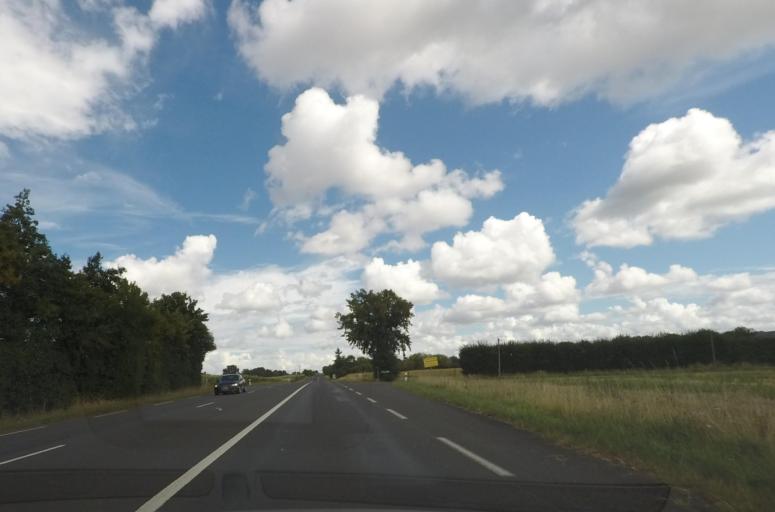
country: FR
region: Pays de la Loire
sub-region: Departement de la Sarthe
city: Clermont-Creans
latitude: 47.7359
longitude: -0.0063
